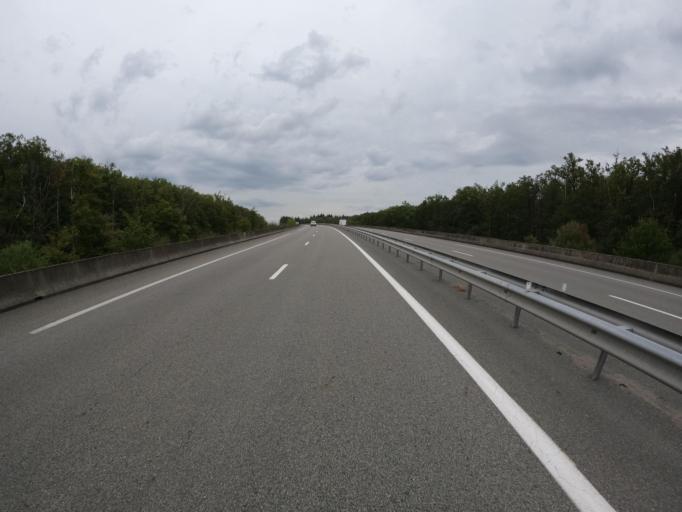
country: FR
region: Limousin
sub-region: Departement de la Creuse
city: Gouzon
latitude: 46.1933
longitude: 2.1710
